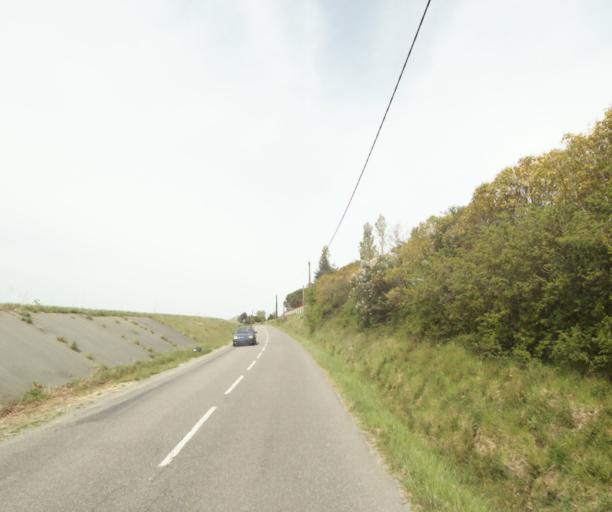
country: FR
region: Midi-Pyrenees
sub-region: Departement de la Haute-Garonne
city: Pechabou
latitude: 43.4895
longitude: 1.4991
